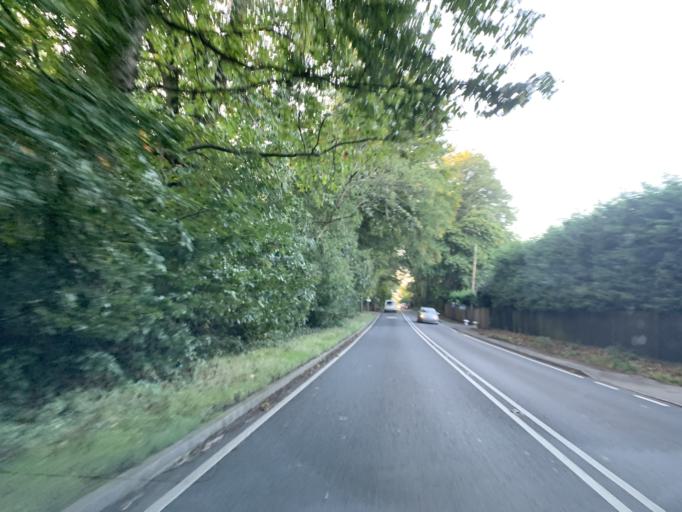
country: GB
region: England
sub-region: Hampshire
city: West Wellow
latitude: 50.9664
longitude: -1.5776
